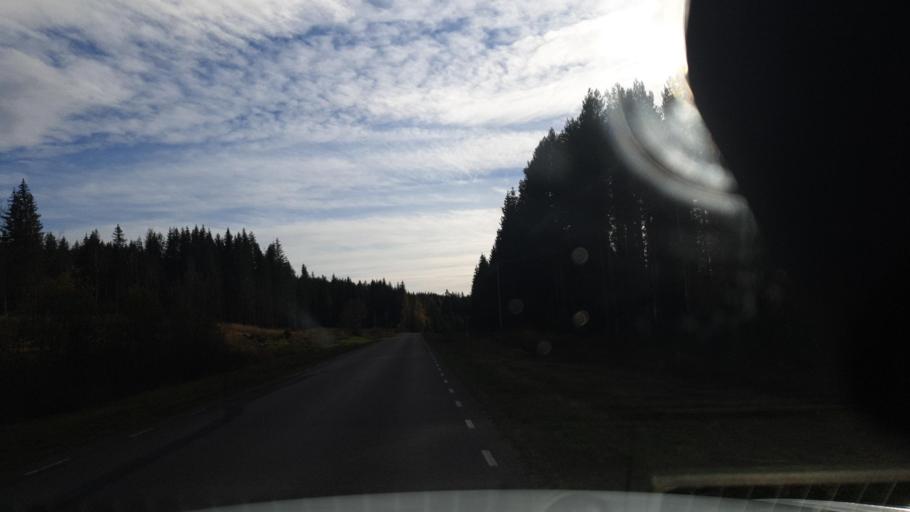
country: SE
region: Vaermland
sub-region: Eda Kommun
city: Charlottenberg
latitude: 59.9447
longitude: 12.3844
